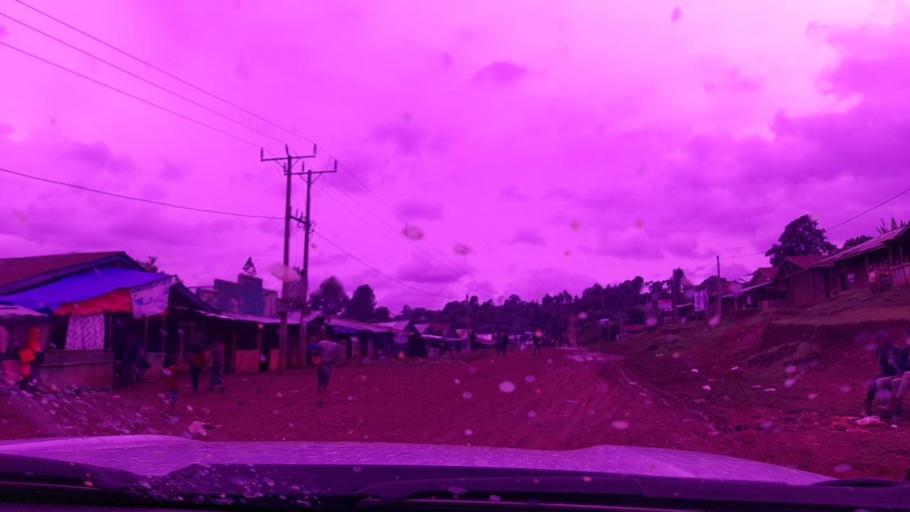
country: ET
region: Southern Nations, Nationalities, and People's Region
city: Tippi
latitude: 7.5682
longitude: 35.6571
